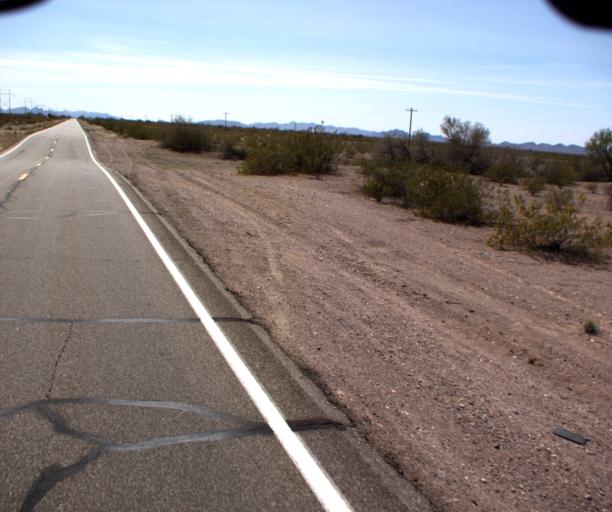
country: US
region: Arizona
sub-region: La Paz County
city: Quartzsite
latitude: 33.4877
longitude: -114.2170
